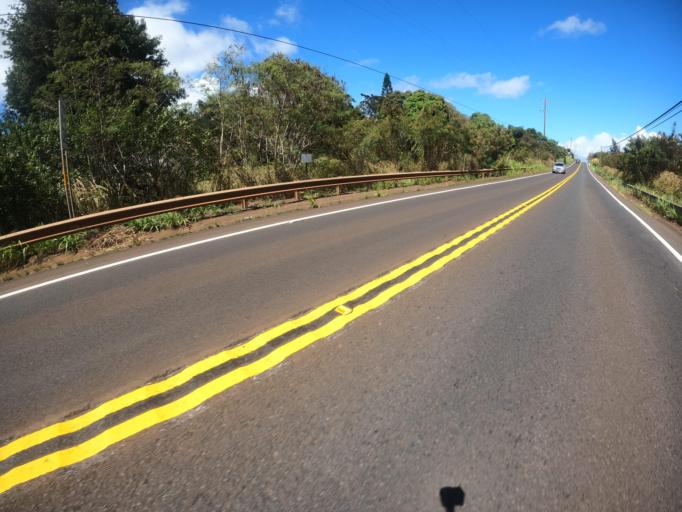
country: US
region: Hawaii
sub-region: Honolulu County
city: Schofield Barracks
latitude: 21.4545
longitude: -158.0593
